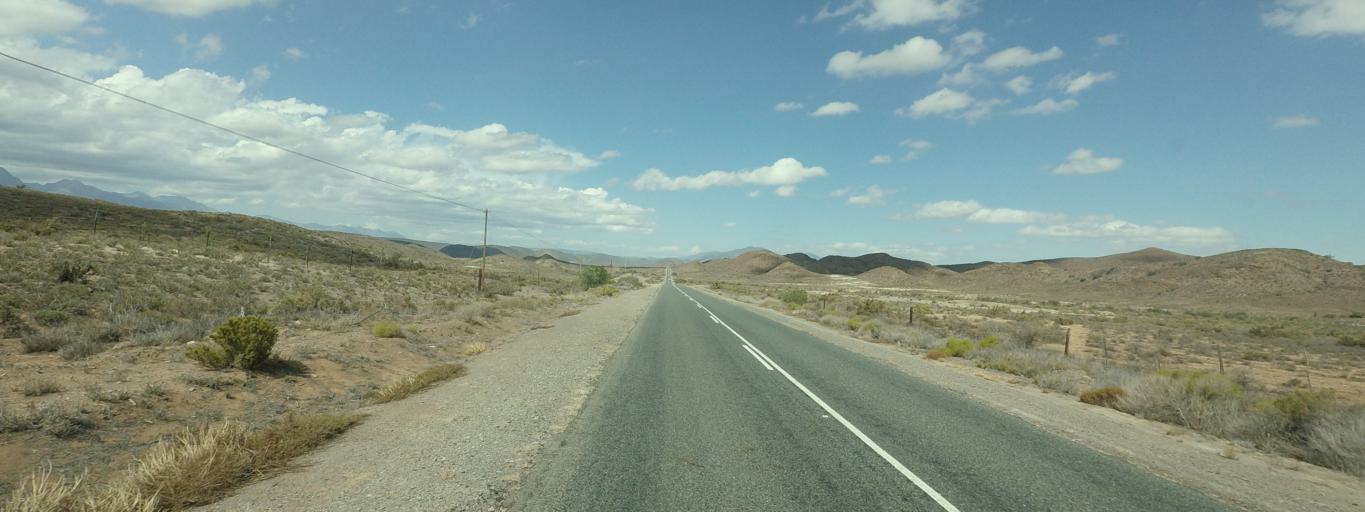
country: ZA
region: Western Cape
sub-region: Eden District Municipality
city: Ladismith
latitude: -33.5996
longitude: 21.0985
